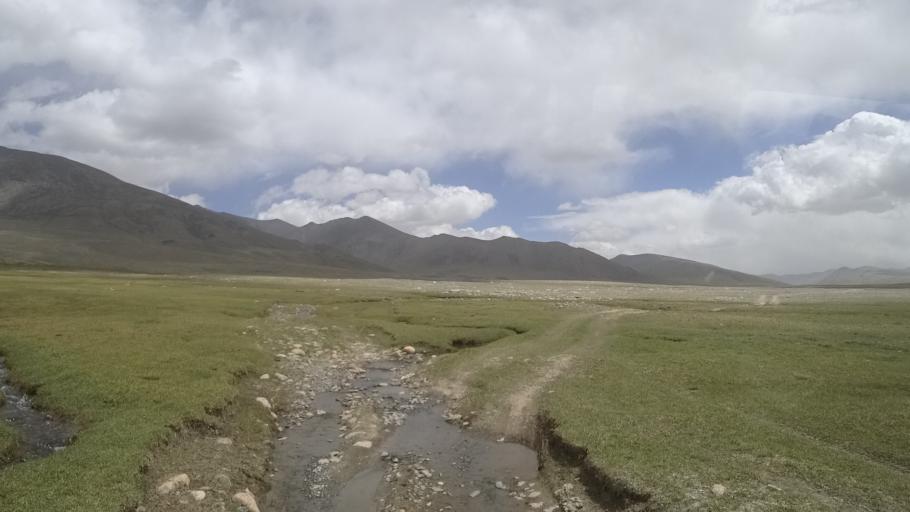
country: TJ
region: Gorno-Badakhshan
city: Murghob
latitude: 37.4871
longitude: 73.9906
